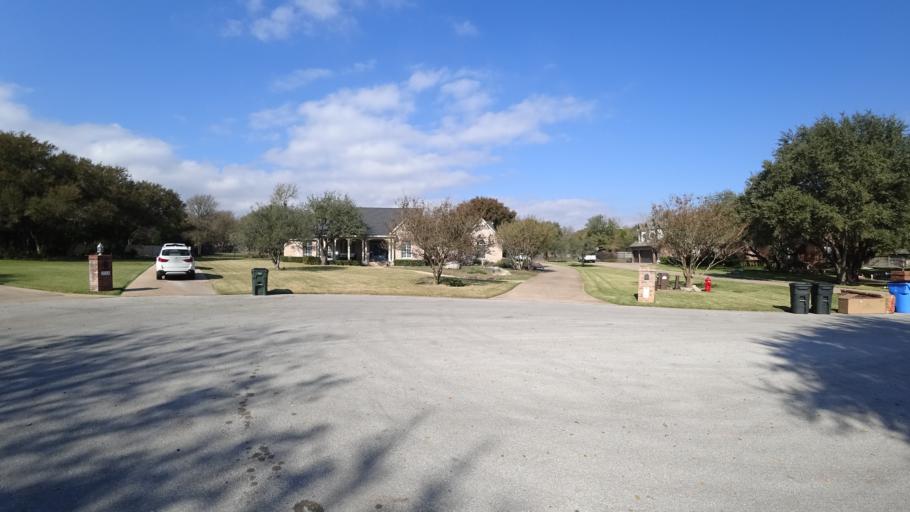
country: US
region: Texas
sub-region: Travis County
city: Shady Hollow
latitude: 30.1582
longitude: -97.8705
